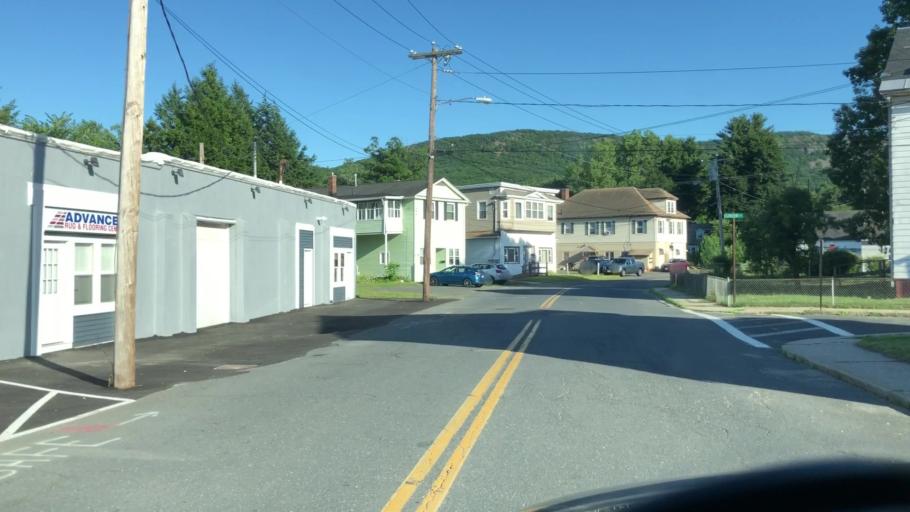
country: US
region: Massachusetts
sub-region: Hampshire County
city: Easthampton
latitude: 42.2721
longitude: -72.6535
